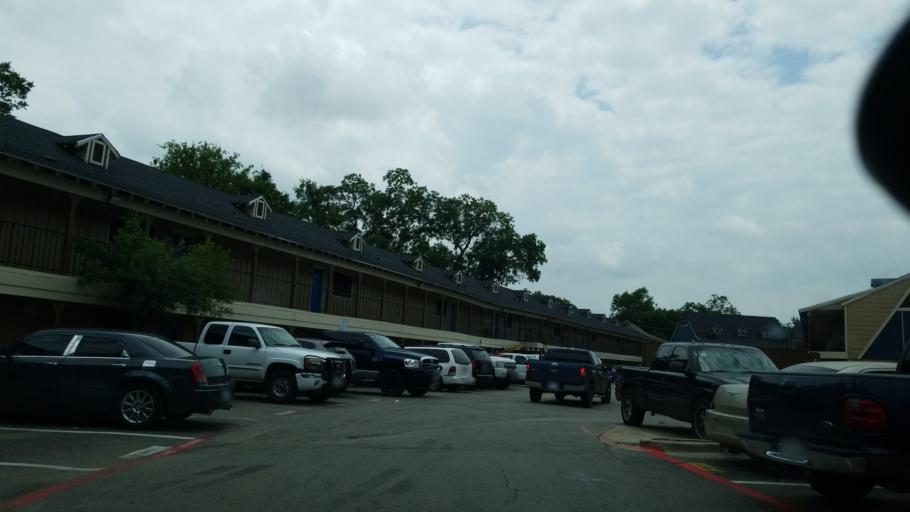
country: US
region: Texas
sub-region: Dallas County
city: Farmers Branch
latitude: 32.8716
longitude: -96.8668
